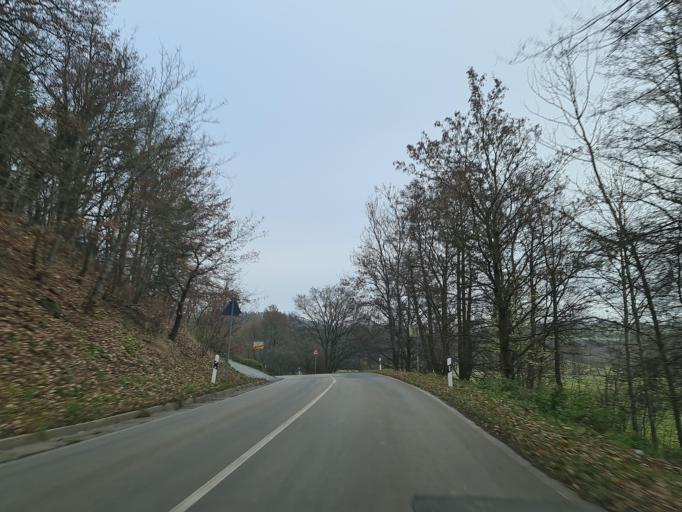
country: DE
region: Saxony
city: Syrau
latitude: 50.5094
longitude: 12.0932
